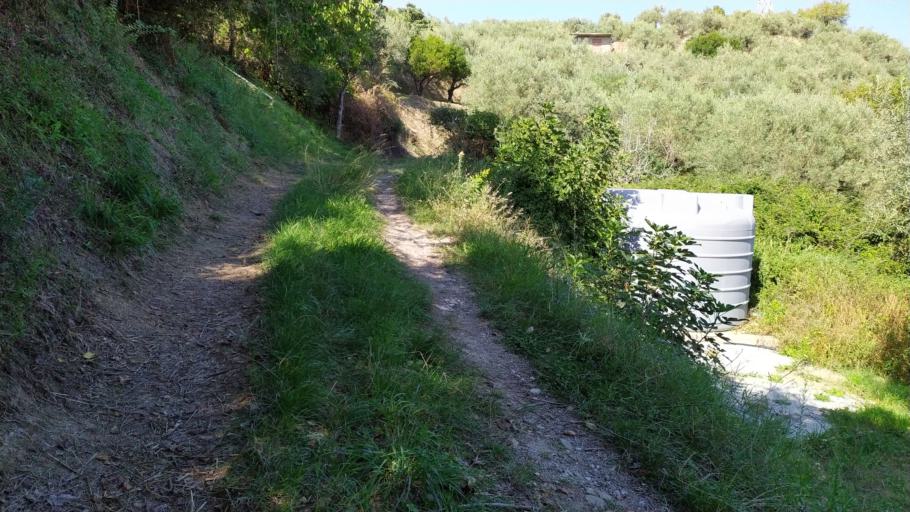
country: IT
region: Sicily
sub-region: Messina
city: Gualtieri Sicamino
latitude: 38.1587
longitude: 15.2979
